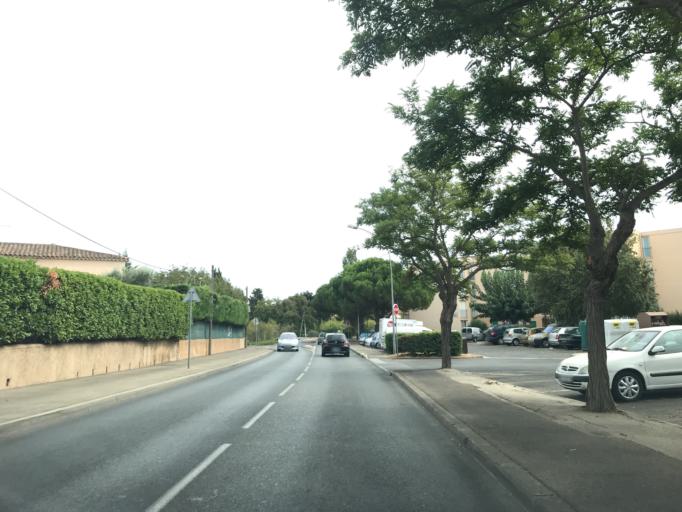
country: FR
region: Provence-Alpes-Cote d'Azur
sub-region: Departement du Var
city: Six-Fours-les-Plages
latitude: 43.0921
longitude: 5.8485
